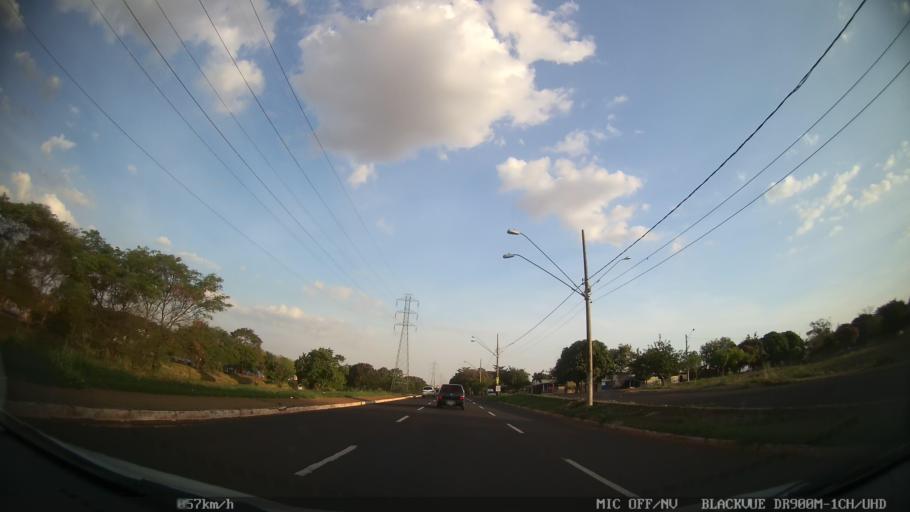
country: BR
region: Sao Paulo
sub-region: Ribeirao Preto
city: Ribeirao Preto
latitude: -21.1225
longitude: -47.8031
